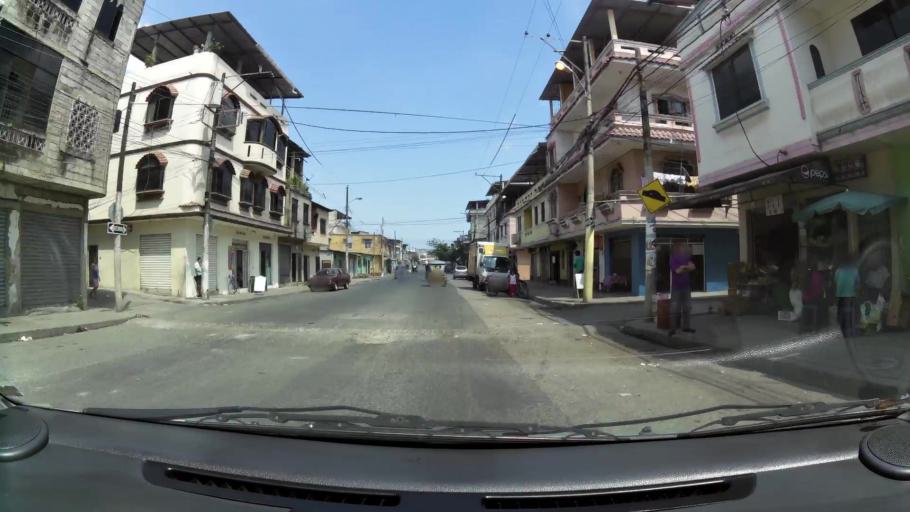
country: EC
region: Guayas
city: Guayaquil
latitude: -2.1222
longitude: -79.9269
